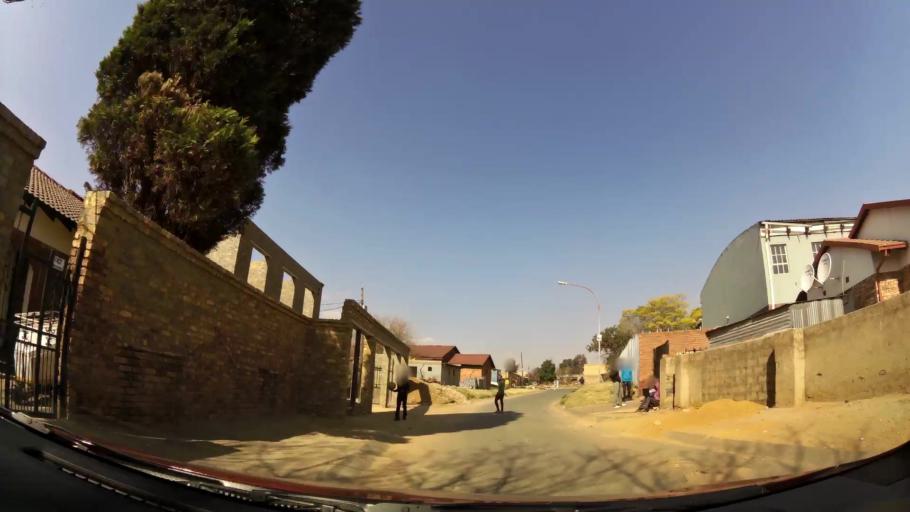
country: ZA
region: Gauteng
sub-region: City of Johannesburg Metropolitan Municipality
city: Johannesburg
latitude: -26.2398
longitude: 27.9580
